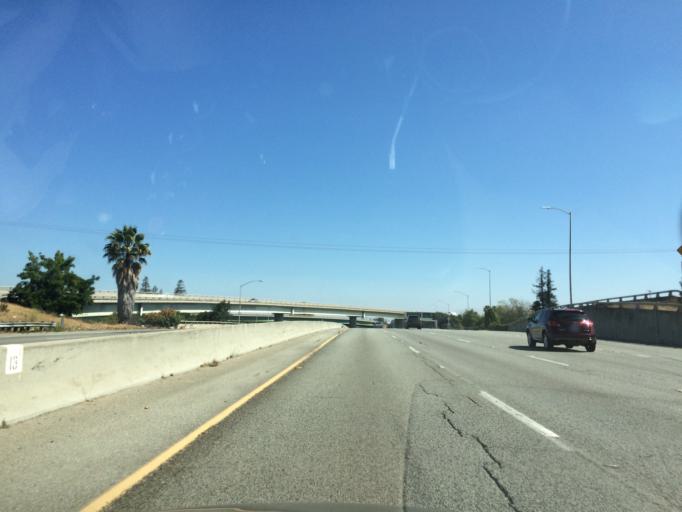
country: US
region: California
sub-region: Santa Clara County
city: Burbank
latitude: 37.3150
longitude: -121.9404
